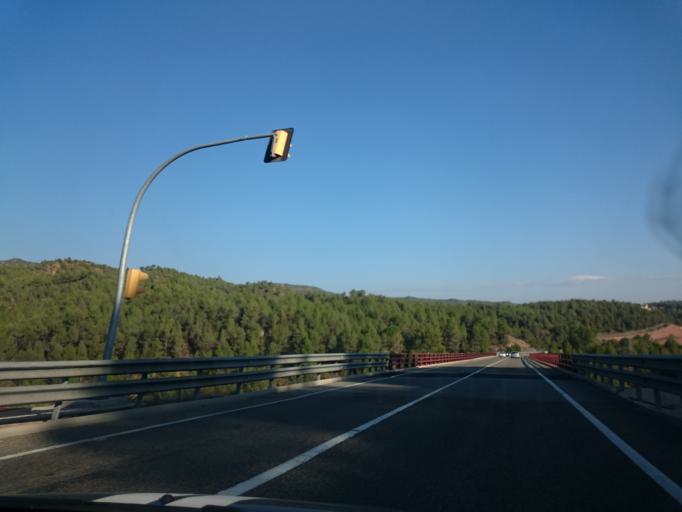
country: ES
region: Catalonia
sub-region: Provincia de Barcelona
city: Sant Salvador de Guardiola
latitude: 41.6830
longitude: 1.7546
